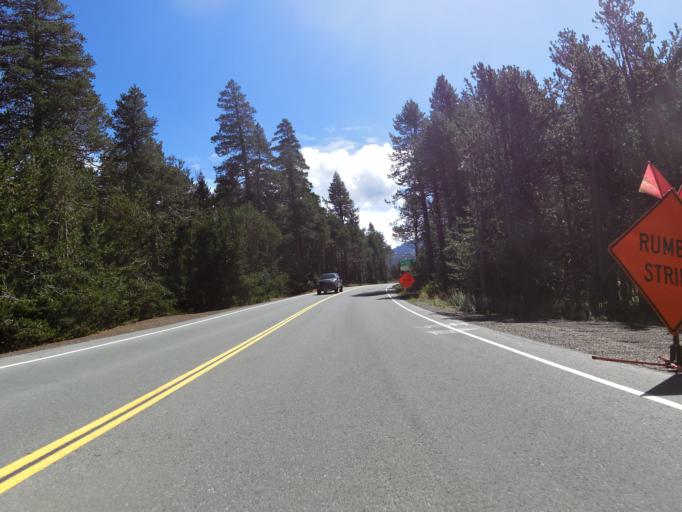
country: US
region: California
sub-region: El Dorado County
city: South Lake Tahoe
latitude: 38.7059
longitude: -120.0401
